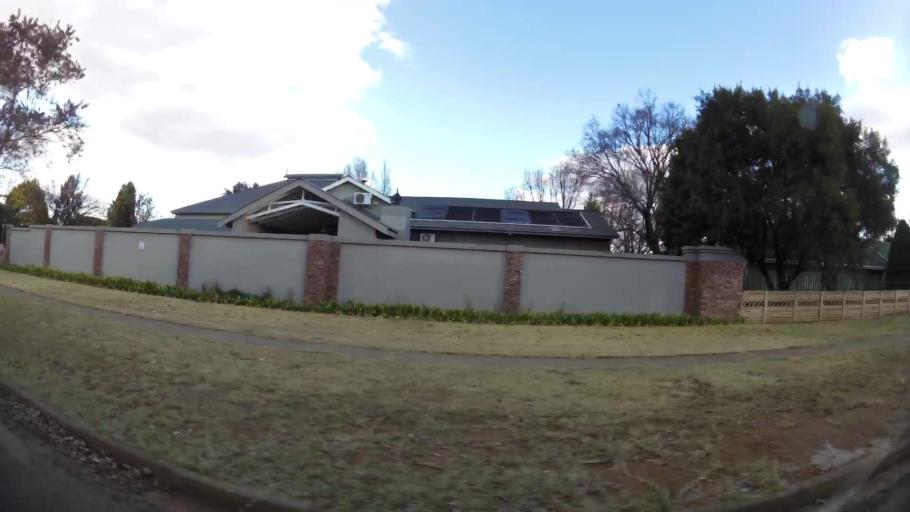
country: ZA
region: North-West
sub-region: Dr Kenneth Kaunda District Municipality
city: Potchefstroom
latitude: -26.7204
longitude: 27.0882
